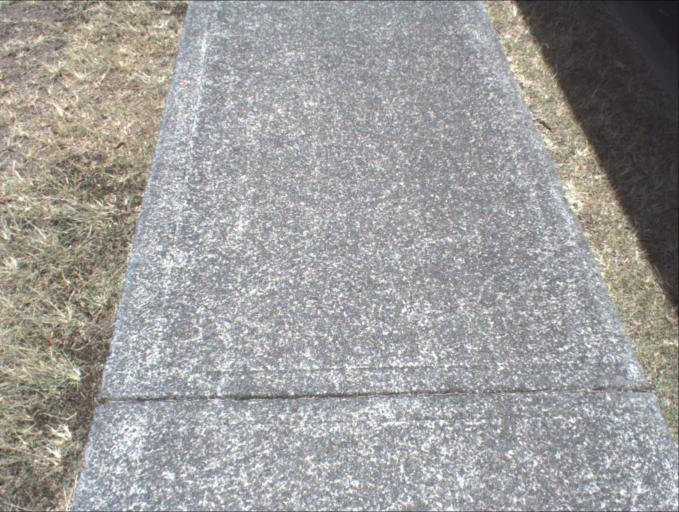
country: AU
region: Queensland
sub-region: Logan
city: Windaroo
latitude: -27.7336
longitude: 153.2132
